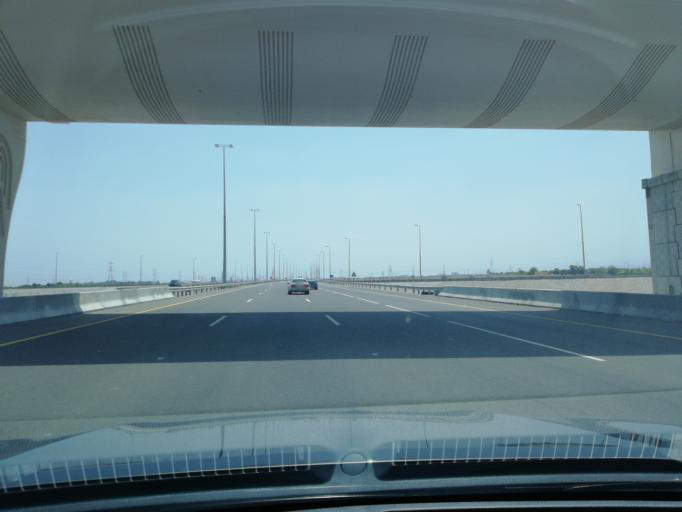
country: OM
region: Al Batinah
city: Barka'
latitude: 23.6311
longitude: 57.9896
